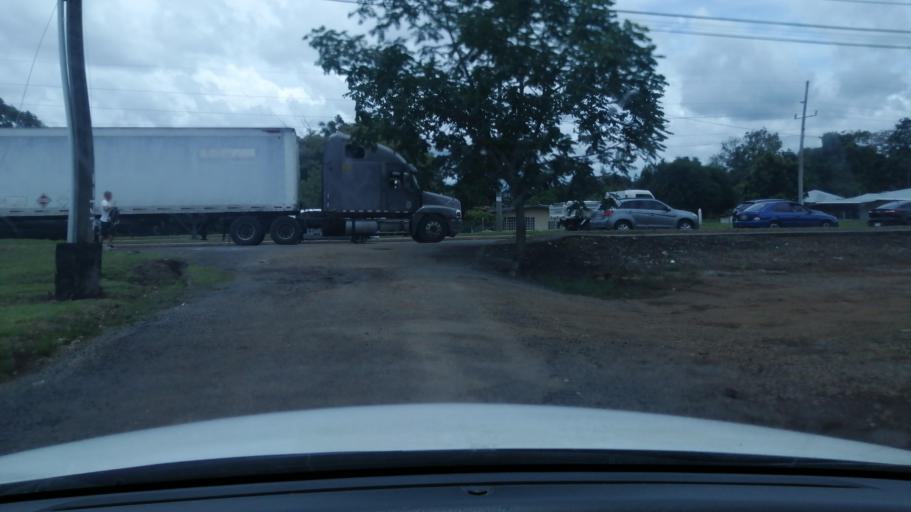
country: PA
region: Chiriqui
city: David
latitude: 8.4274
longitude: -82.4473
